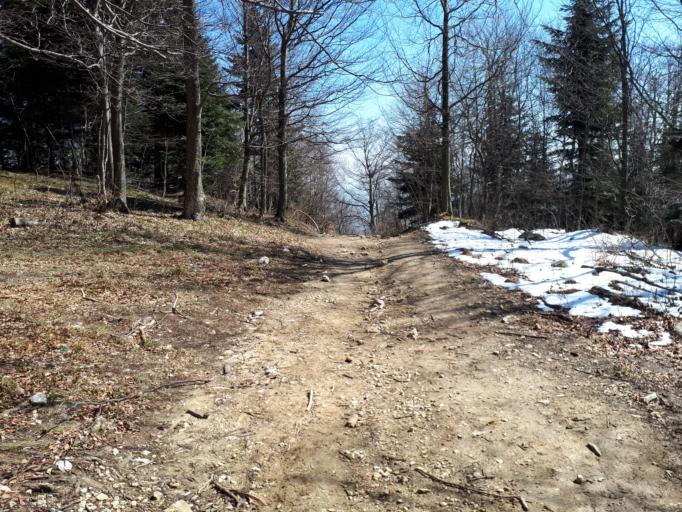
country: HR
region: Varazdinska
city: Ivanec
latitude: 46.1792
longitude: 16.1360
